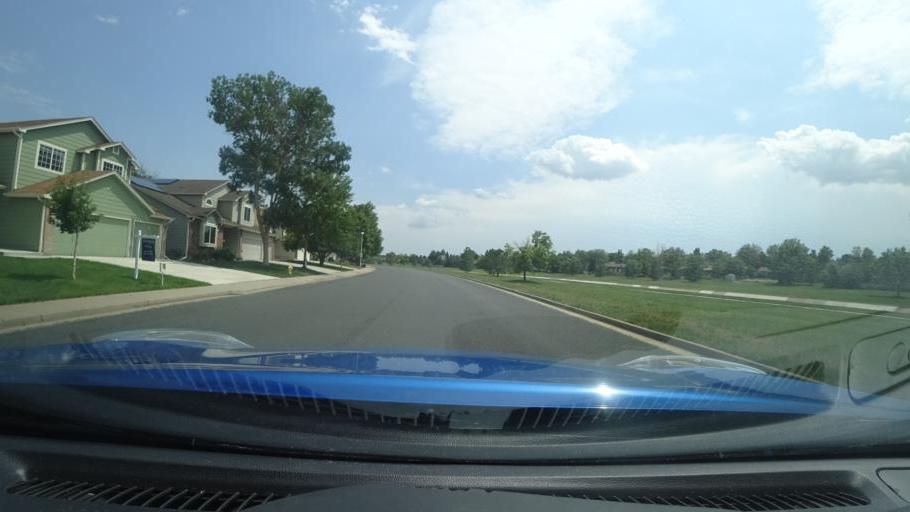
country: US
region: Colorado
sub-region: Adams County
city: Aurora
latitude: 39.6711
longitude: -104.7834
